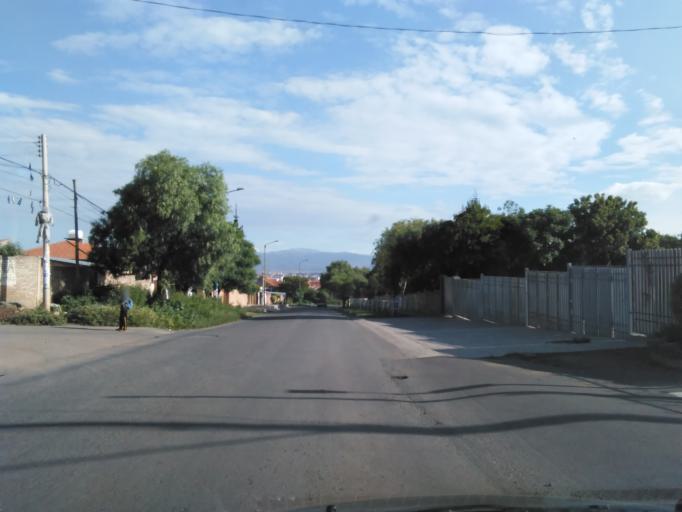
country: BO
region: Cochabamba
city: Cochabamba
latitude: -17.3467
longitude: -66.1831
